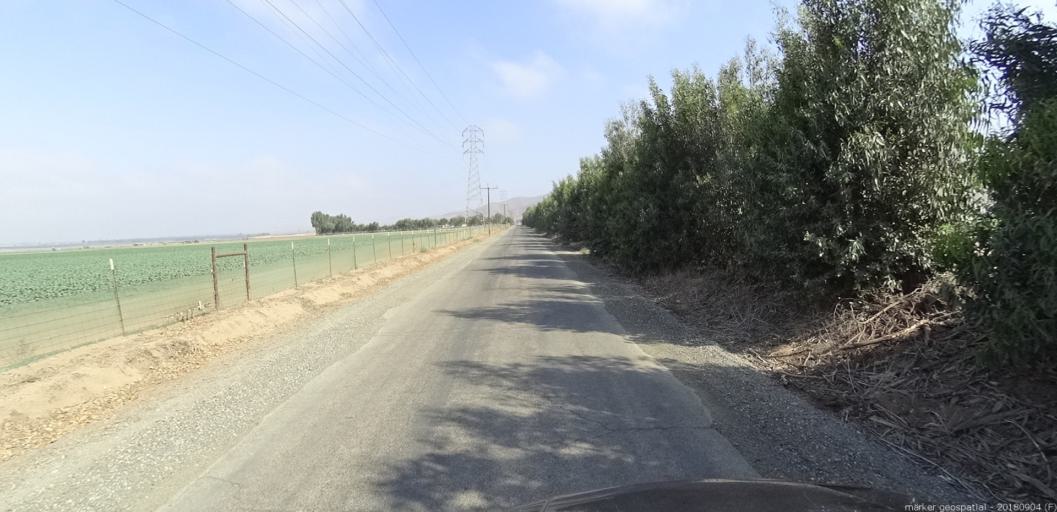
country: US
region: California
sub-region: Monterey County
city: Soledad
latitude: 36.4512
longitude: -121.3318
